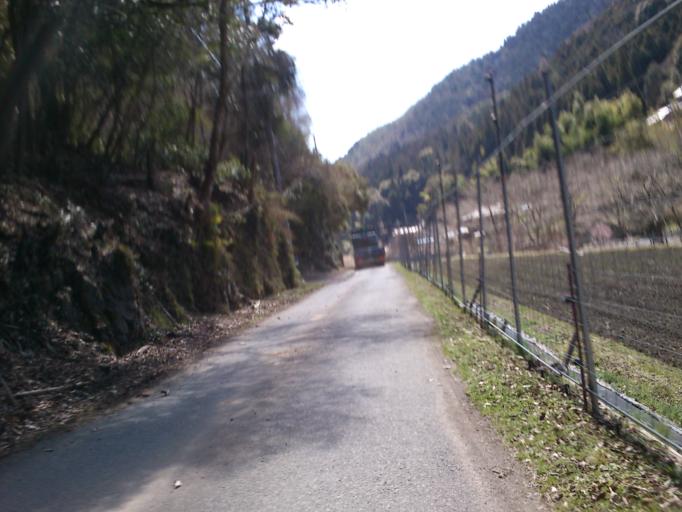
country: JP
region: Shiga Prefecture
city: Otsu-shi
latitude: 34.9435
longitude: 135.8506
